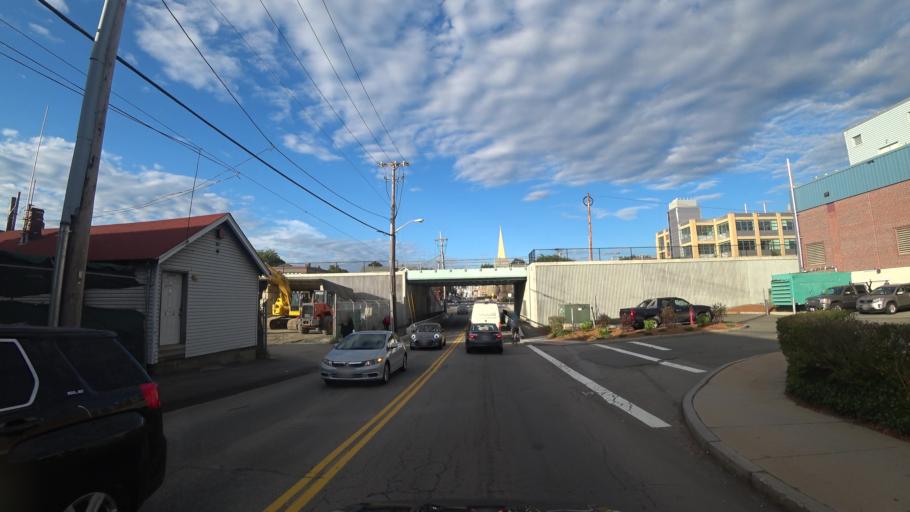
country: US
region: Massachusetts
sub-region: Middlesex County
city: Medford
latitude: 42.4033
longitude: -71.1126
